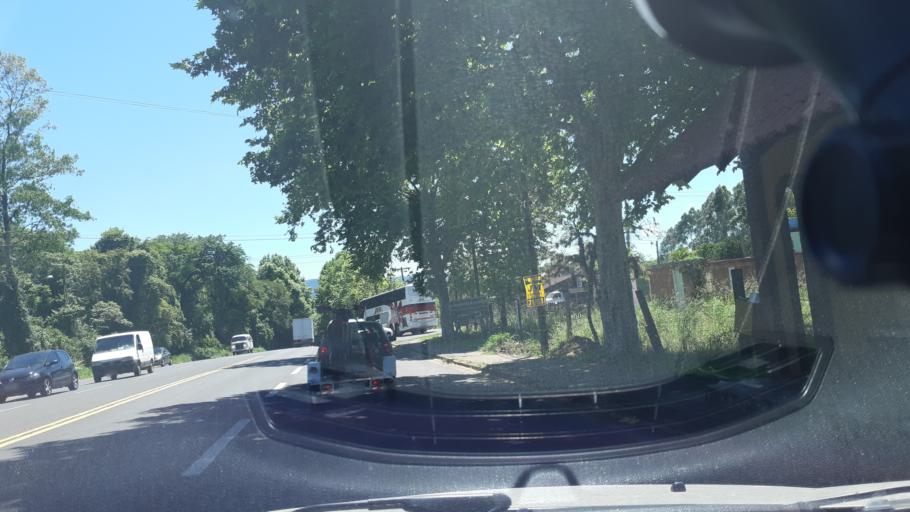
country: BR
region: Rio Grande do Sul
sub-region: Ivoti
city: Ivoti
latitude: -29.6193
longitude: -51.1222
